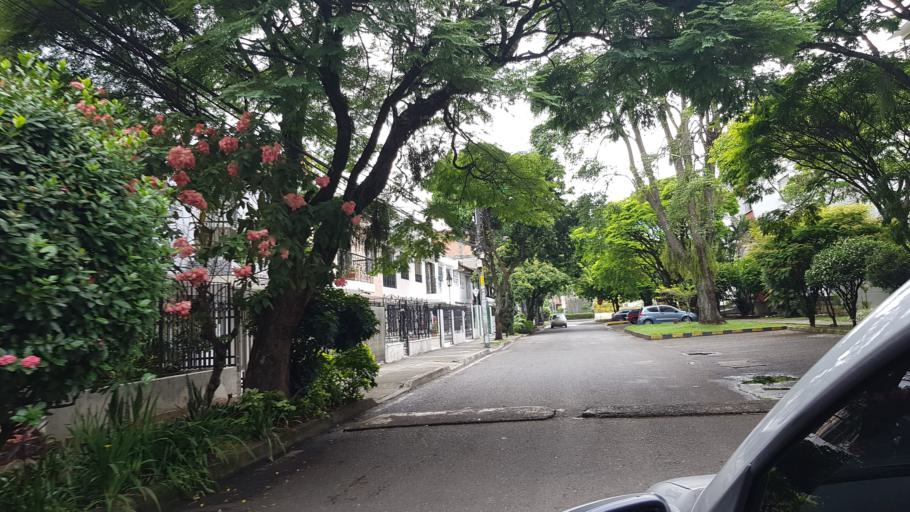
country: CO
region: Valle del Cauca
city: Cali
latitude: 3.3888
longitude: -76.5432
